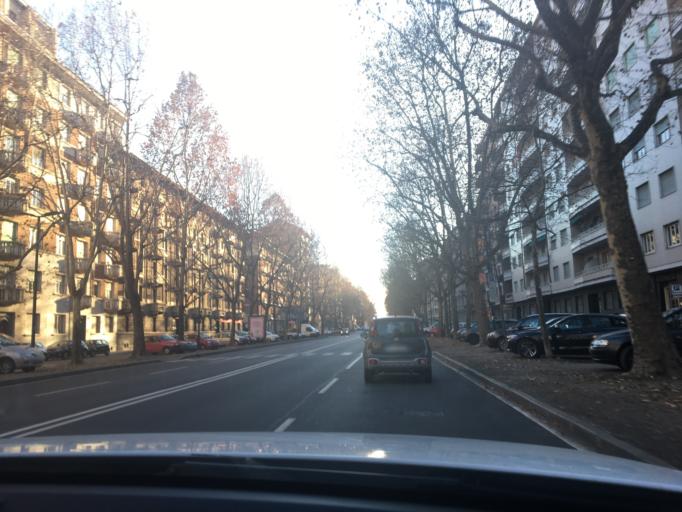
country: IT
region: Piedmont
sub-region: Provincia di Torino
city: Turin
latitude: 45.0538
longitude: 7.6627
